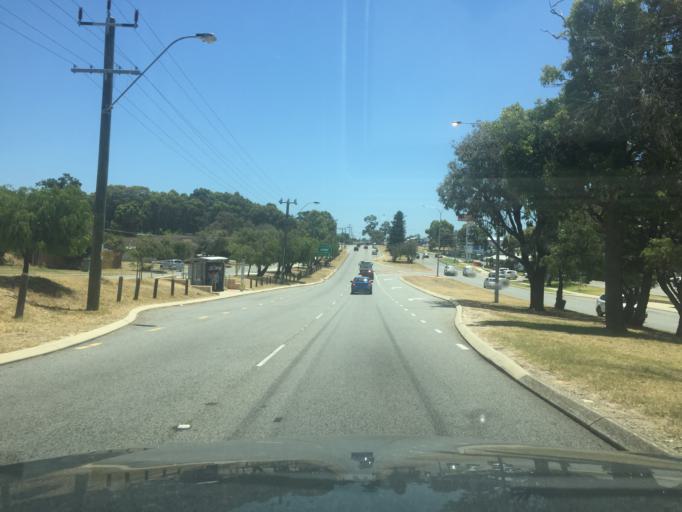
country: AU
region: Western Australia
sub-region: Fremantle
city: Samson
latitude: -32.0646
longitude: 115.7971
